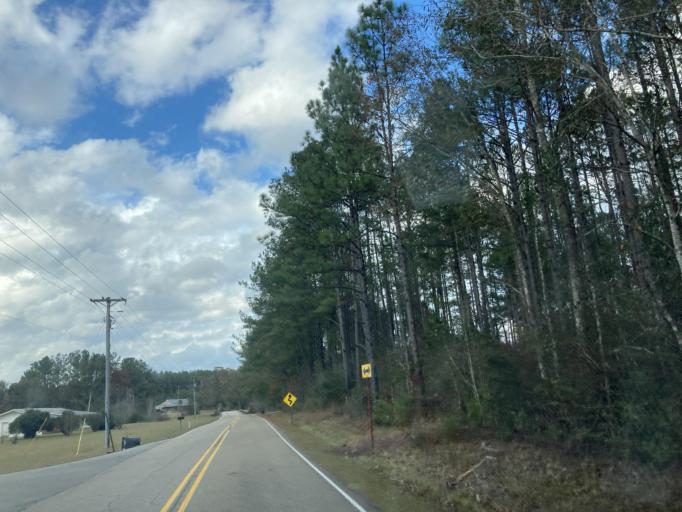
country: US
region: Mississippi
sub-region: Lamar County
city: Purvis
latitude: 31.1627
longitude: -89.5896
